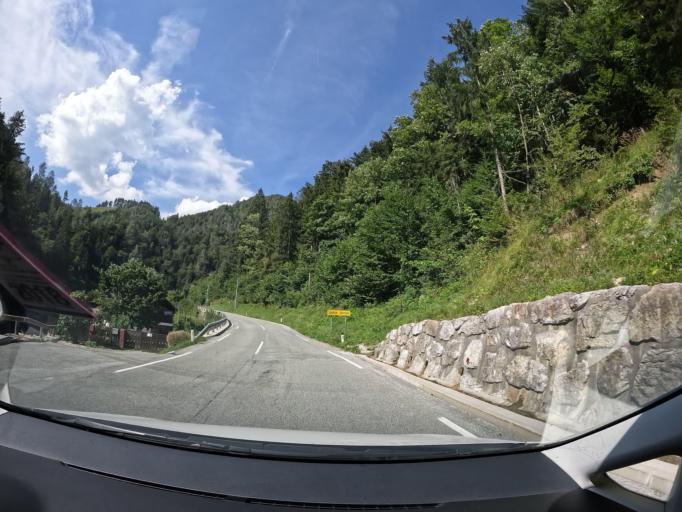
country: SI
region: Trzic
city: Trzic
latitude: 46.4070
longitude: 14.3128
